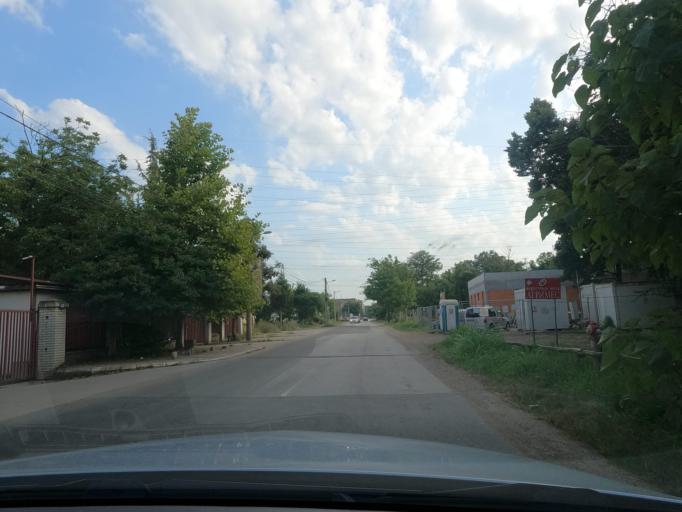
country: RS
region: Central Serbia
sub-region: Belgrade
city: Zemun
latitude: 44.8232
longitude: 20.3804
